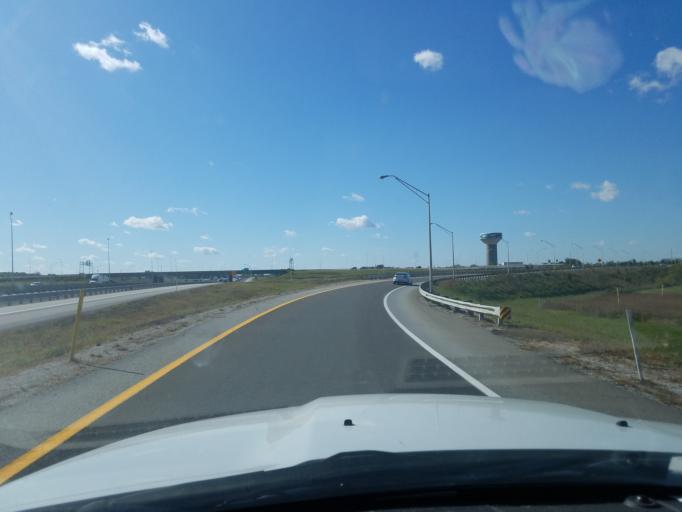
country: US
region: Kentucky
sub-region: Warren County
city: Plano
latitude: 36.9135
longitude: -86.4309
